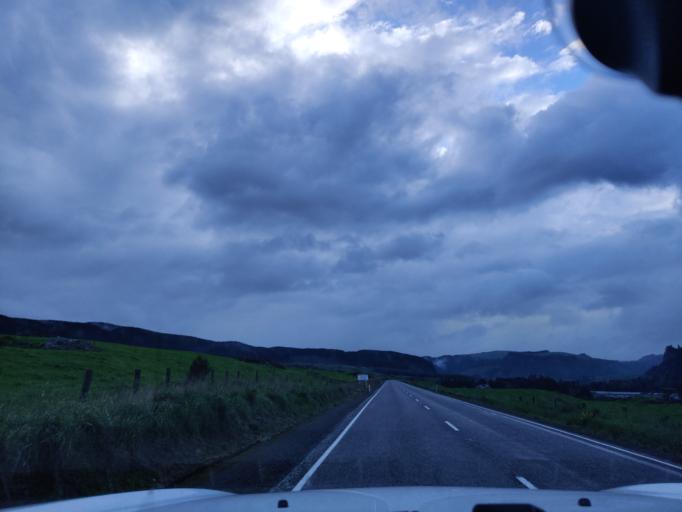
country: NZ
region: Waikato
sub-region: South Waikato District
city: Tokoroa
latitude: -38.4106
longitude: 175.8008
